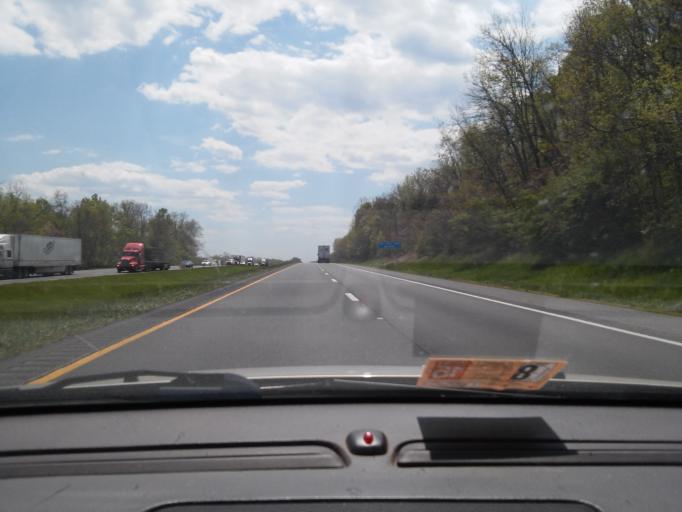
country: US
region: West Virginia
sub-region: Berkeley County
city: Inwood
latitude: 39.3251
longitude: -78.0701
